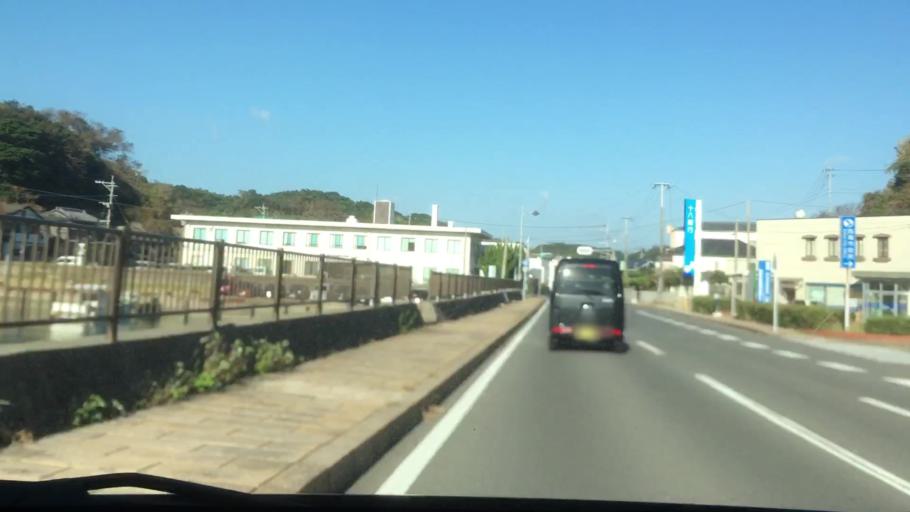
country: JP
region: Nagasaki
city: Togitsu
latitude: 32.9324
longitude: 129.6430
